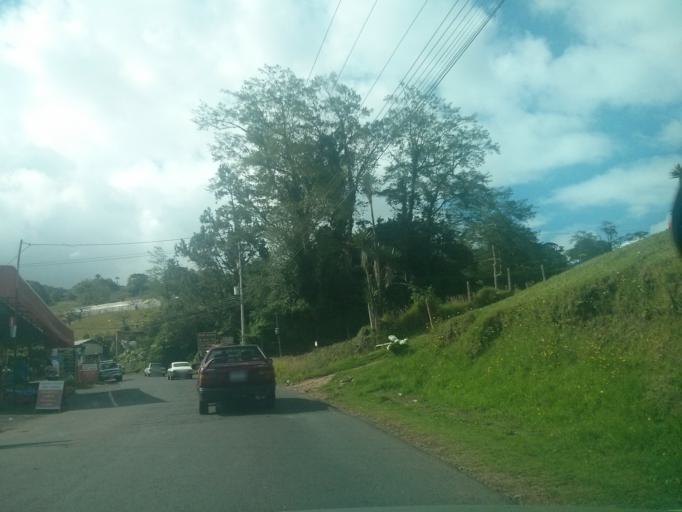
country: CR
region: Alajuela
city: Sabanilla
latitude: 10.1620
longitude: -84.1990
